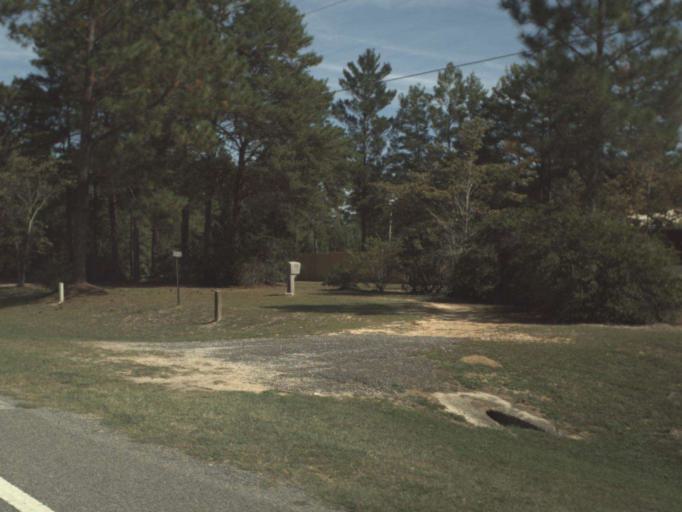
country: US
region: Florida
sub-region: Washington County
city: Chipley
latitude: 30.5868
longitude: -85.5920
